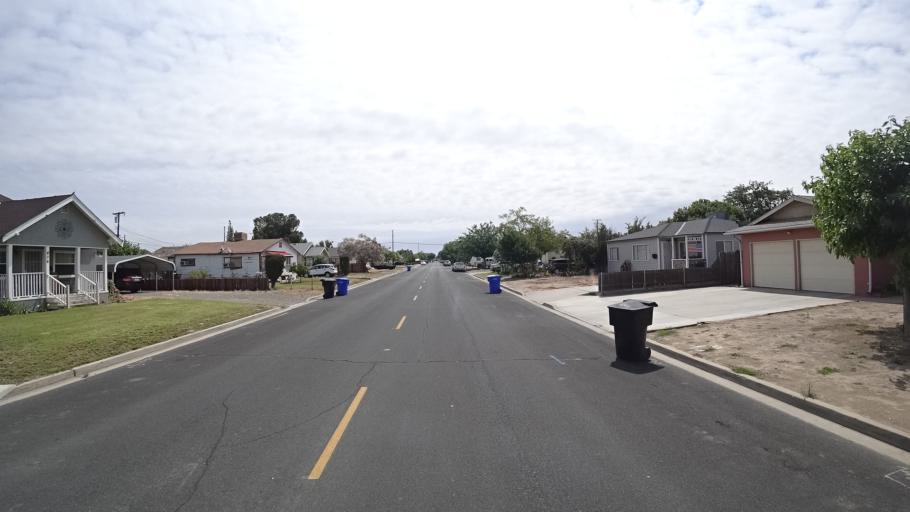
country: US
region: California
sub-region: Kings County
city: Hanford
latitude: 36.3340
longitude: -119.6407
